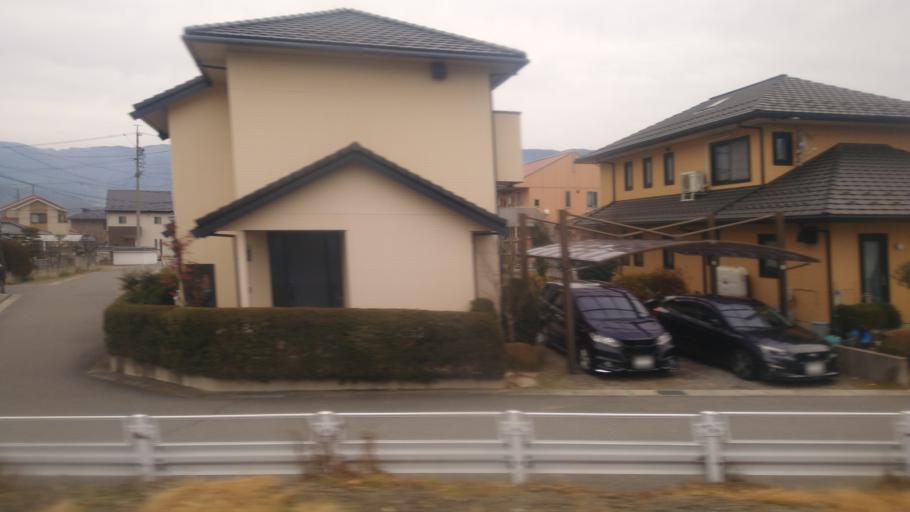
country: JP
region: Nagano
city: Matsumoto
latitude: 36.1854
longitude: 137.9604
